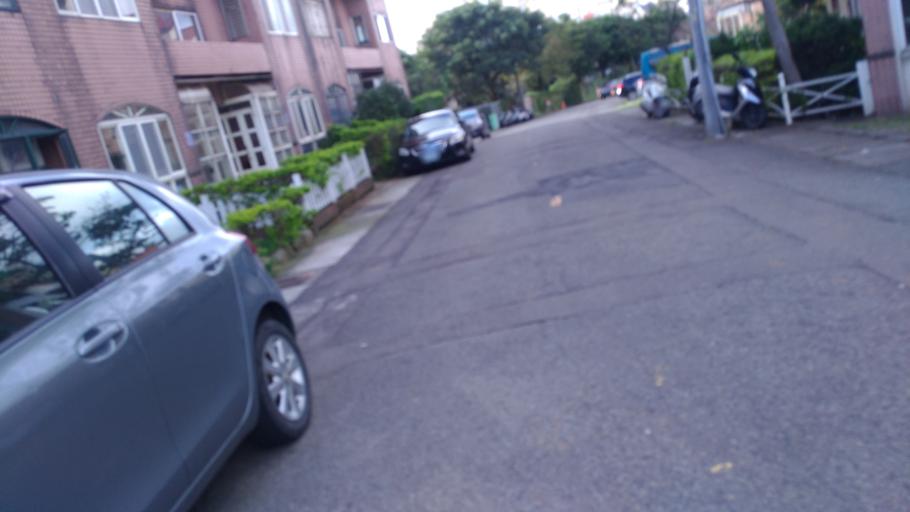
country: TW
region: Taiwan
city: Daxi
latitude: 24.8837
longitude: 121.1730
